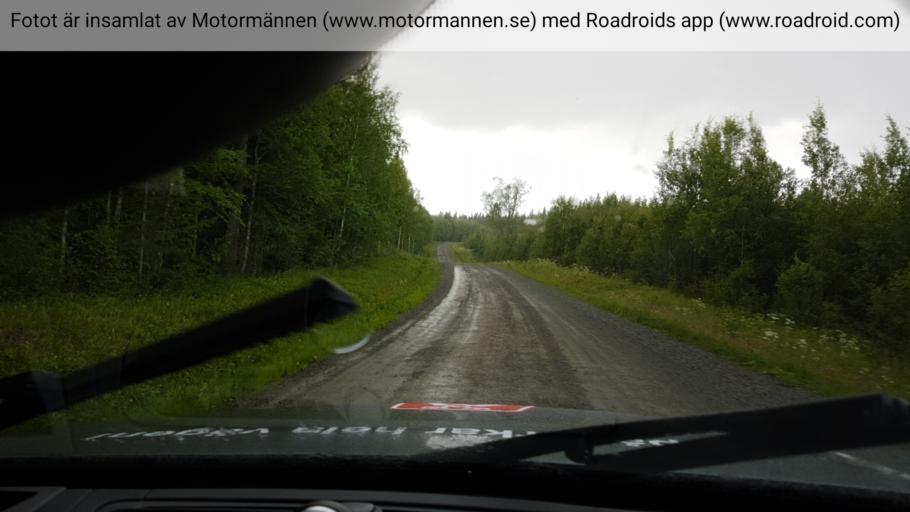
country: SE
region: Jaemtland
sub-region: Bergs Kommun
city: Hoverberg
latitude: 62.9838
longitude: 14.1886
